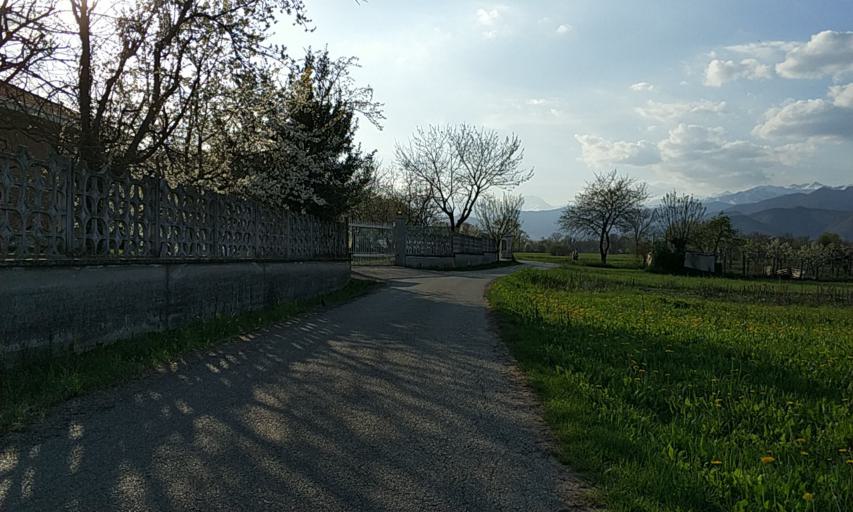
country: IT
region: Piedmont
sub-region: Provincia di Torino
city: San Carlo Canavese
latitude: 45.2424
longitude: 7.5924
